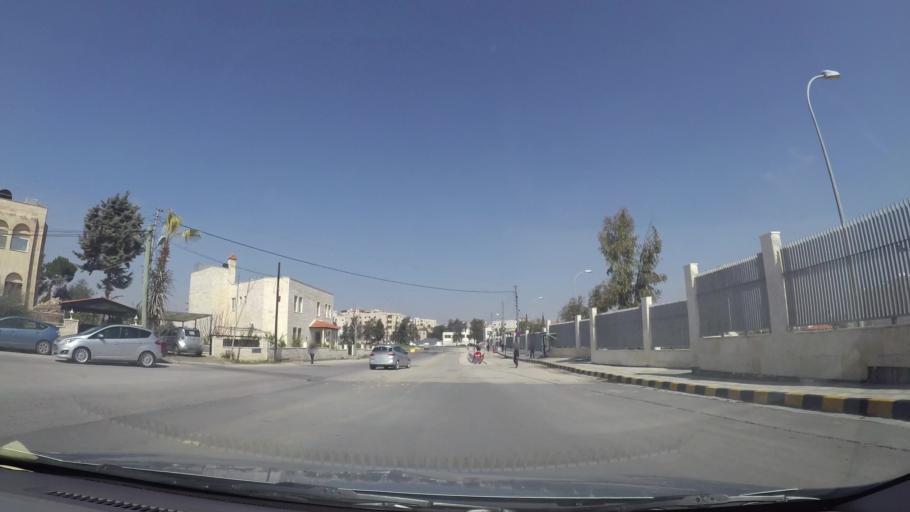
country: JO
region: Amman
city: Al Bunayyat ash Shamaliyah
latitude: 31.9004
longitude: 35.8745
